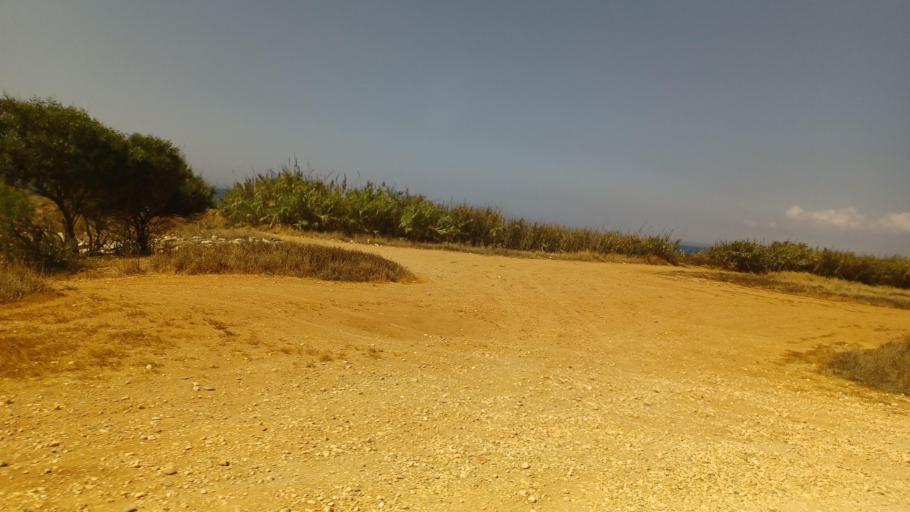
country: CY
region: Larnaka
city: Xylotymbou
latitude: 34.9772
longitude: 33.7863
